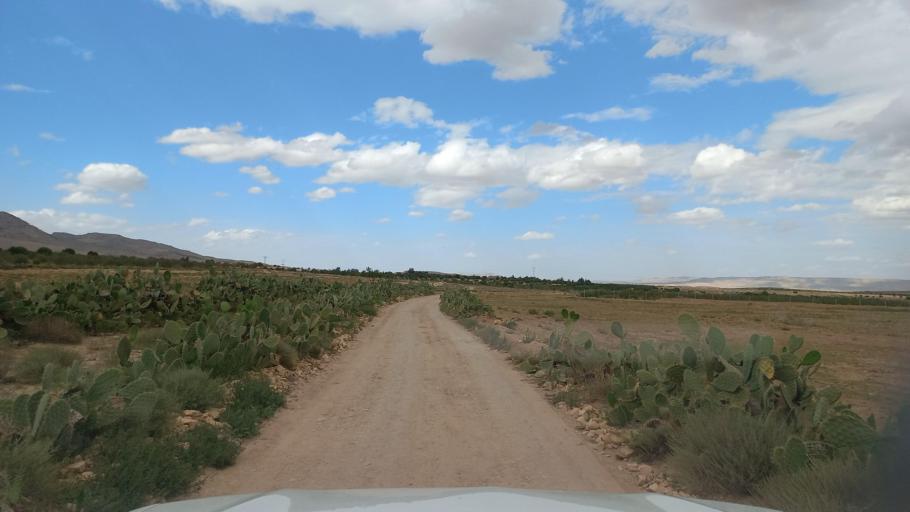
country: TN
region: Al Qasrayn
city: Sbiba
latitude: 35.4340
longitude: 9.0978
